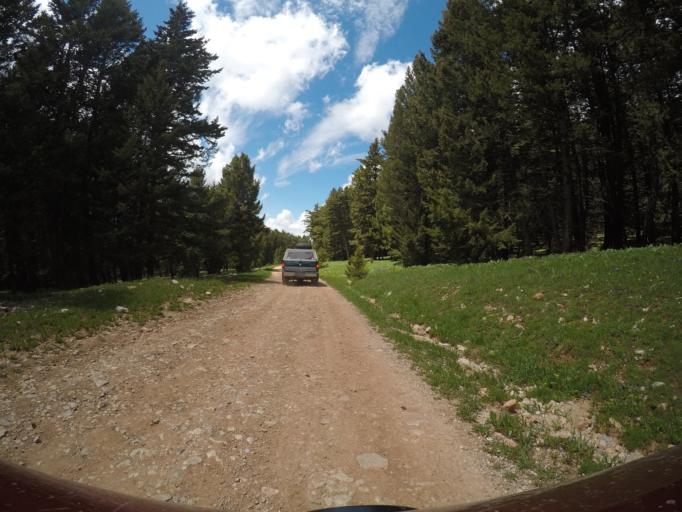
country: US
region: Wyoming
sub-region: Big Horn County
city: Lovell
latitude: 45.1632
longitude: -108.4044
